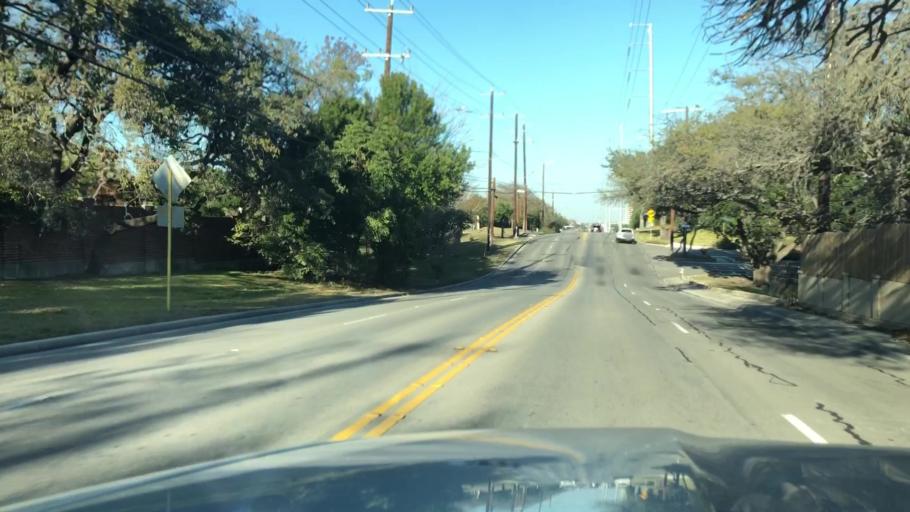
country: US
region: Texas
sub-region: Bexar County
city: Balcones Heights
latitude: 29.4994
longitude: -98.5641
